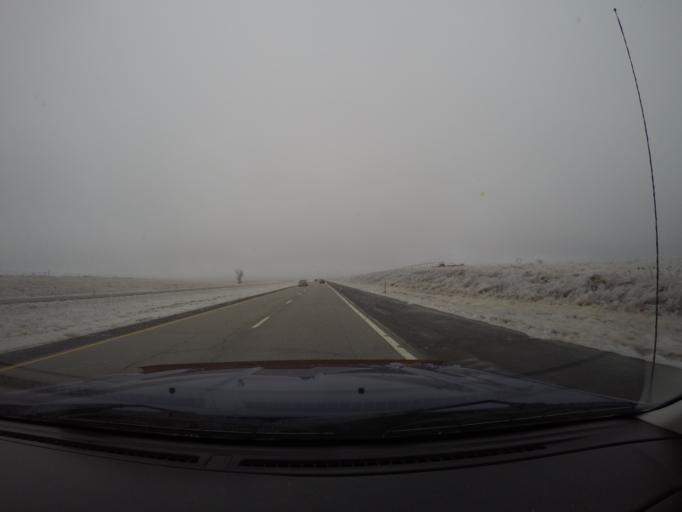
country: US
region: Kansas
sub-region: Riley County
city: Manhattan
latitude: 39.0966
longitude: -96.5381
